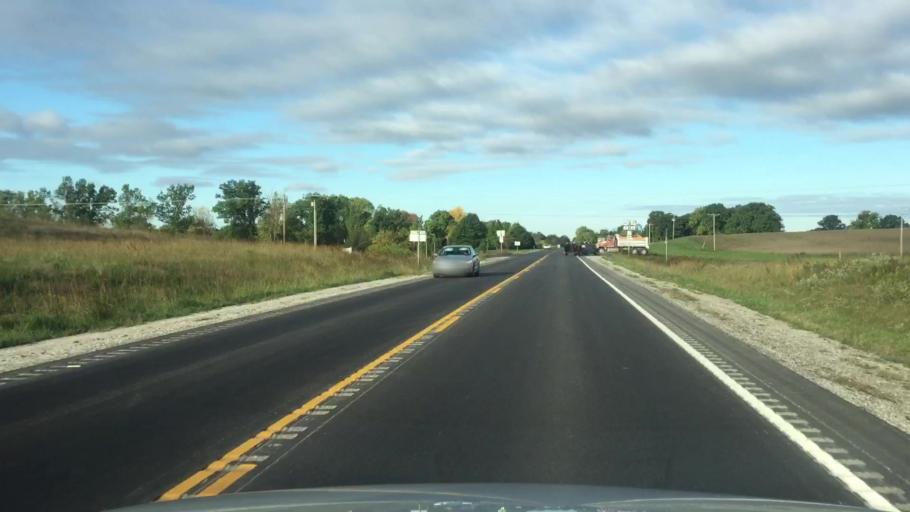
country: US
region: Missouri
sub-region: Boone County
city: Columbia
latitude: 38.9892
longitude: -92.4935
